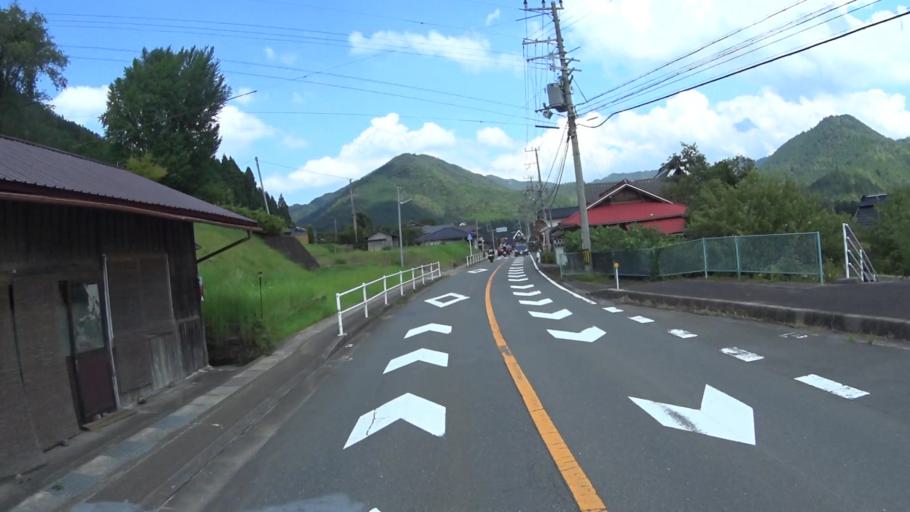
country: JP
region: Fukui
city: Obama
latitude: 35.2768
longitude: 135.5832
